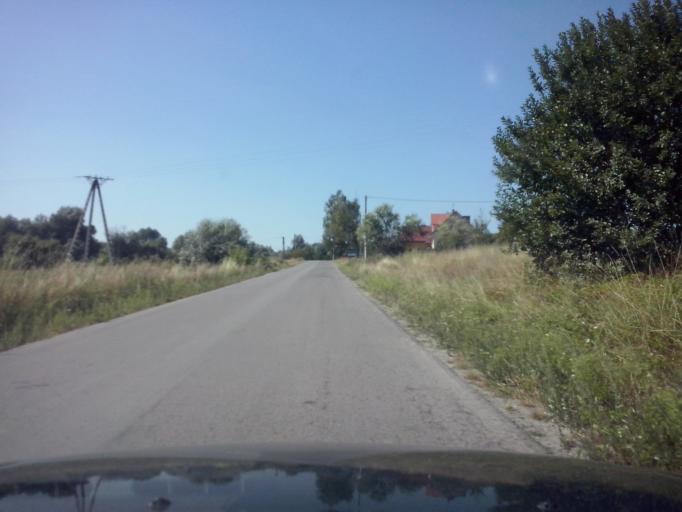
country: PL
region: Swietokrzyskie
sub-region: Powiat kielecki
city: Chmielnik
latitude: 50.6110
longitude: 20.7671
